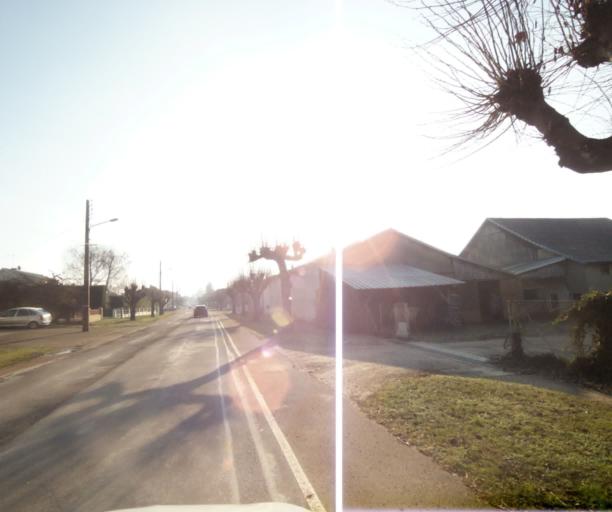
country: FR
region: Champagne-Ardenne
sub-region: Departement de la Haute-Marne
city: Montier-en-Der
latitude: 48.4830
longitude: 4.7636
